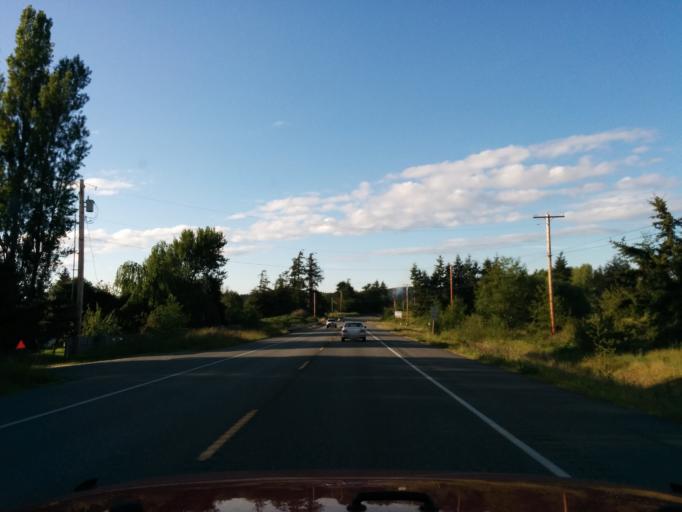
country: US
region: Washington
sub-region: Island County
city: Ault Field
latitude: 48.3831
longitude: -122.6502
